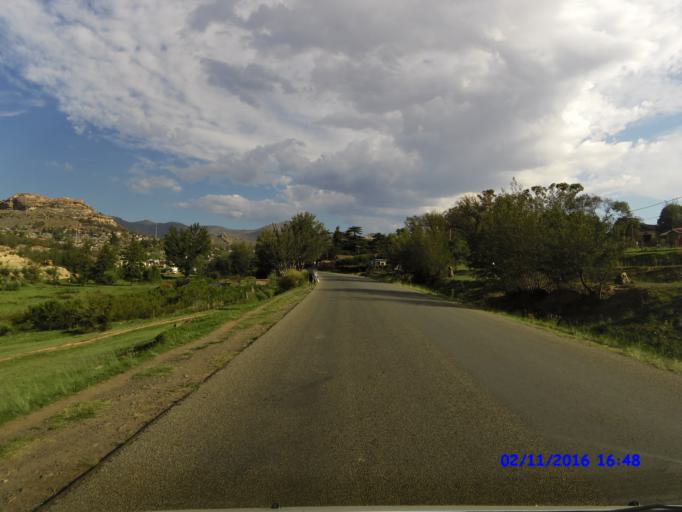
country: LS
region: Butha-Buthe
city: Butha-Buthe
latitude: -28.7616
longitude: 28.2496
